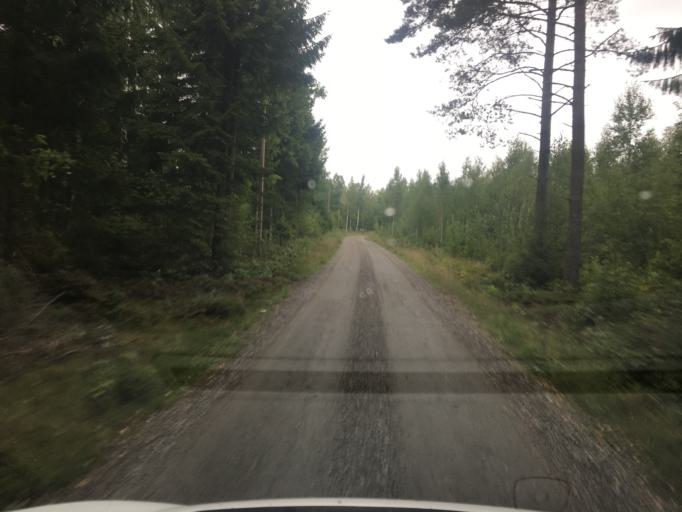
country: SE
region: Kronoberg
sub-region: Ljungby Kommun
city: Lagan
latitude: 56.9693
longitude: 14.0406
